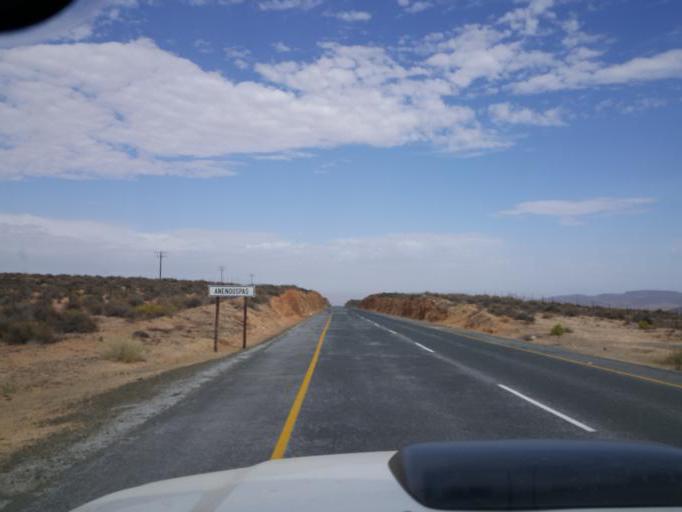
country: ZA
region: Northern Cape
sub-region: Namakwa District Municipality
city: Springbok
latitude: -29.2231
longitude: 17.6590
